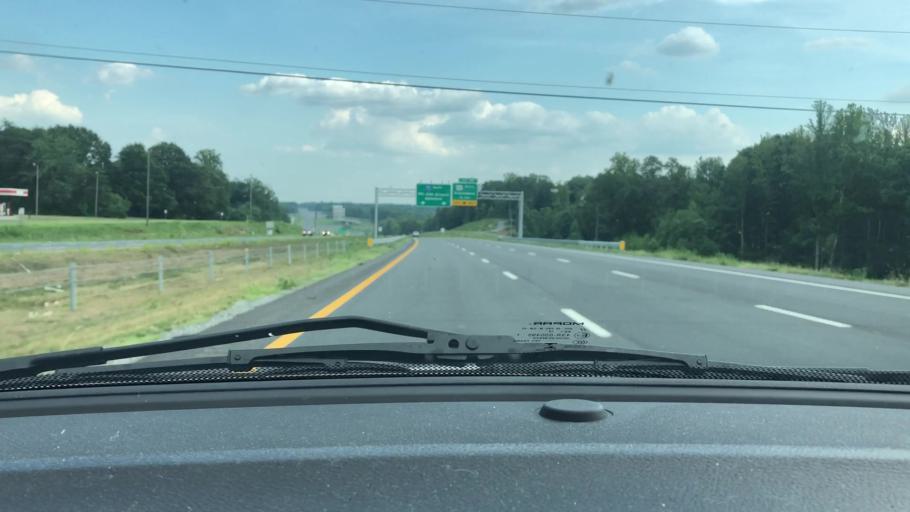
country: US
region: North Carolina
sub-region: Guilford County
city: Summerfield
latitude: 36.2393
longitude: -79.9189
